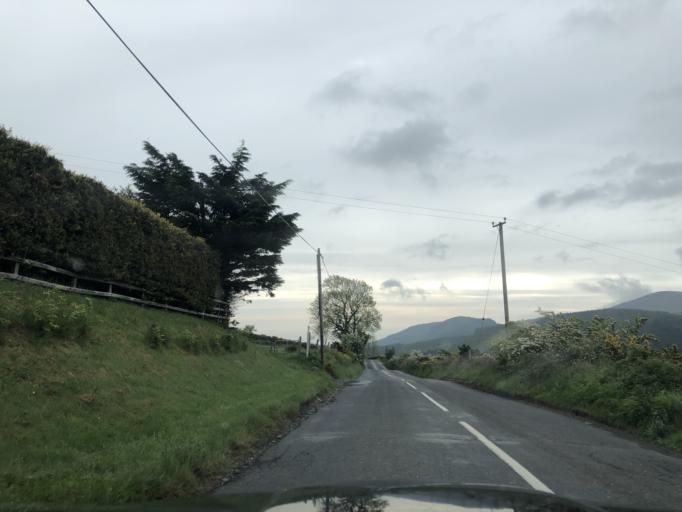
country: GB
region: Northern Ireland
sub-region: Down District
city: Castlewellan
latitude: 54.2205
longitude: -5.9902
